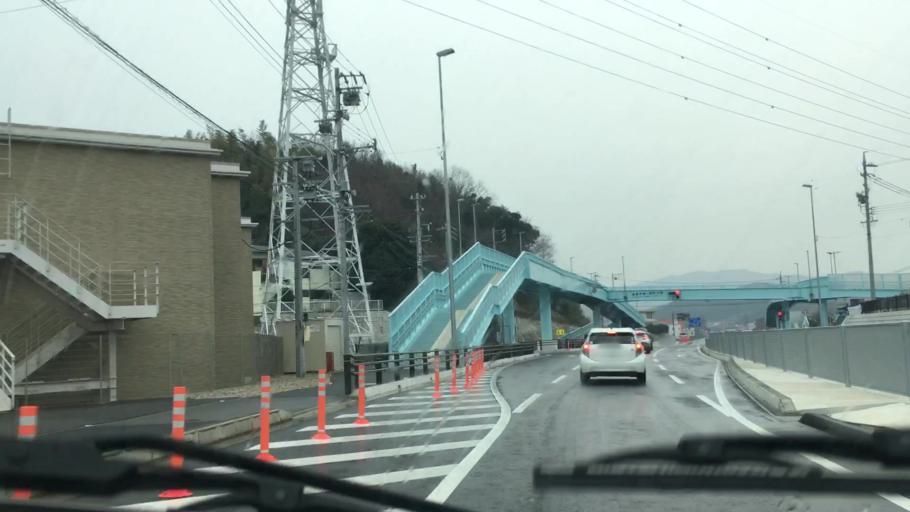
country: JP
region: Aichi
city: Gamagori
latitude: 34.8317
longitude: 137.2161
